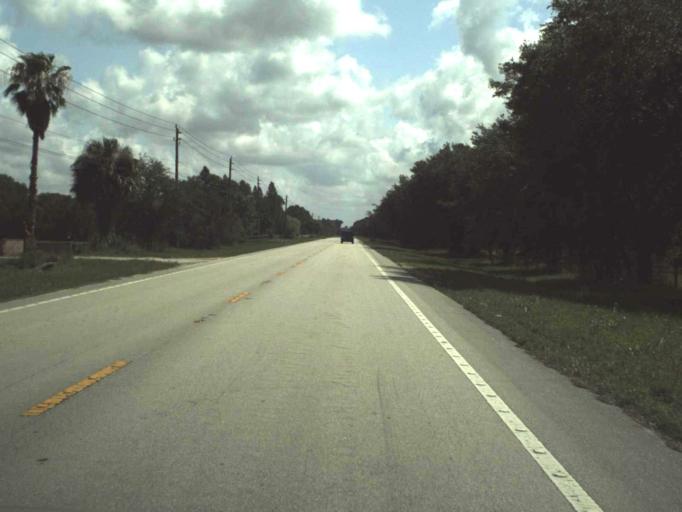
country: US
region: Florida
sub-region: Volusia County
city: Lake Helen
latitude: 28.9098
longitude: -81.1266
